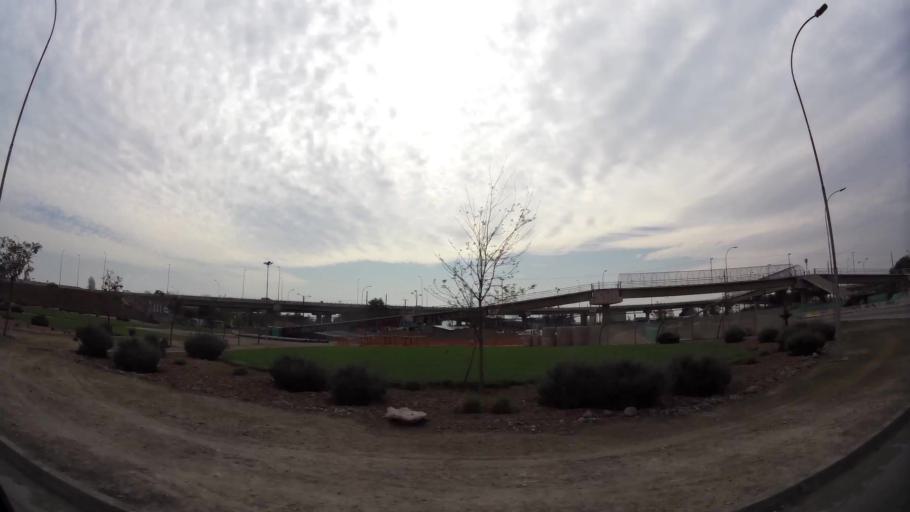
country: CL
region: Santiago Metropolitan
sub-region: Provincia de Maipo
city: San Bernardo
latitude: -33.5280
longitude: -70.7555
